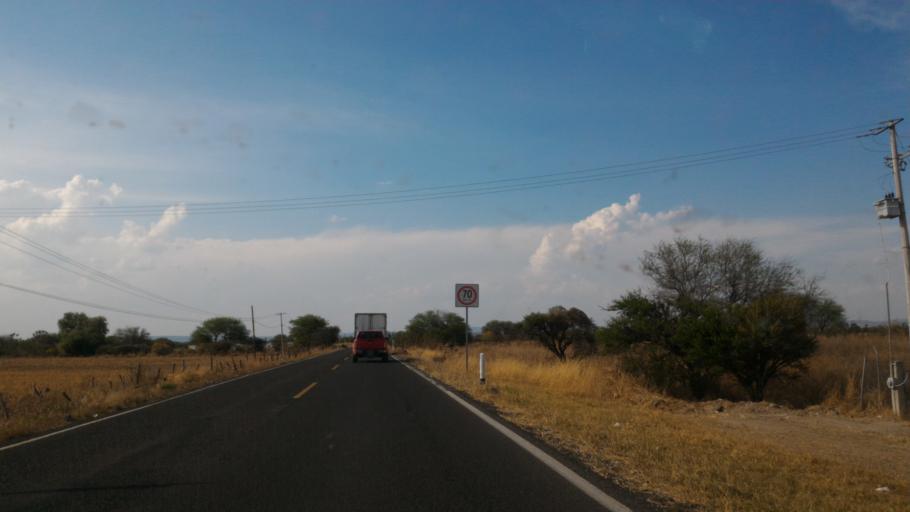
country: MX
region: Guanajuato
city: Ciudad Manuel Doblado
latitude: 20.7624
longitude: -101.9686
